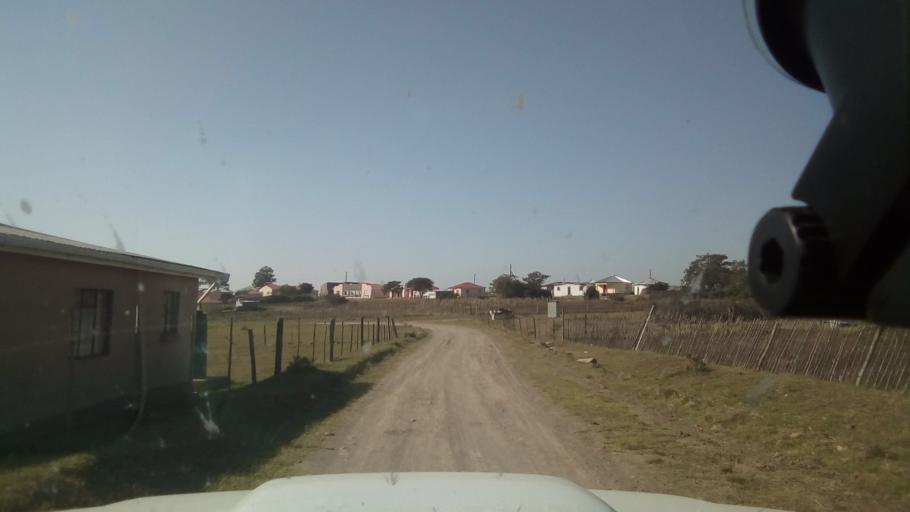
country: ZA
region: Eastern Cape
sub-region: Buffalo City Metropolitan Municipality
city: Bhisho
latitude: -32.9384
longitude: 27.3346
